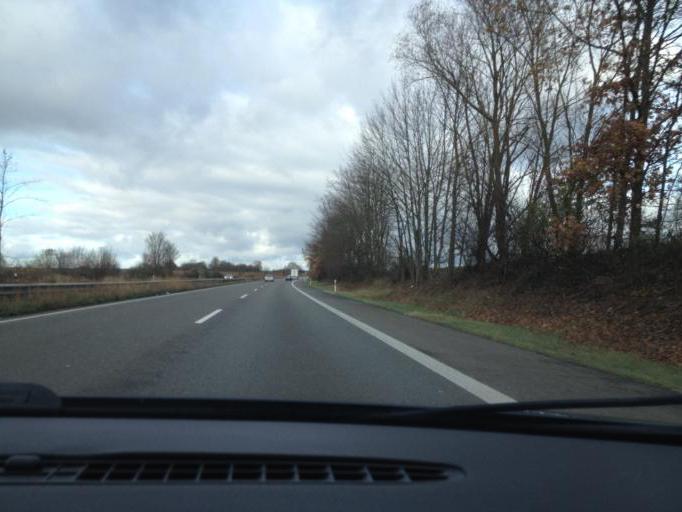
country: DE
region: Rheinland-Pfalz
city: Lingenfeld
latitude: 49.2520
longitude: 8.3317
